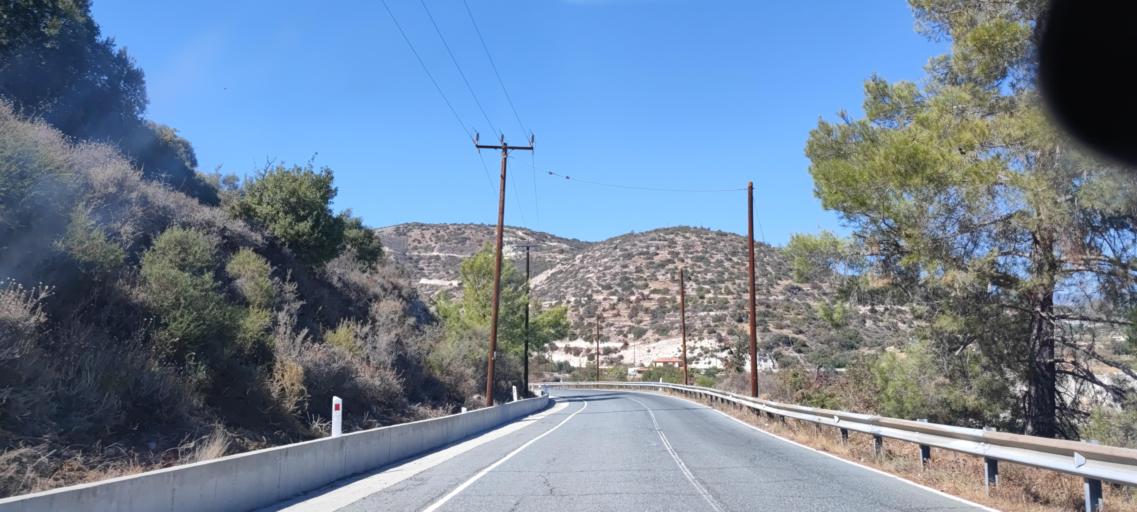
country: CY
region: Limassol
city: Mouttagiaka
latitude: 34.7682
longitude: 33.0553
